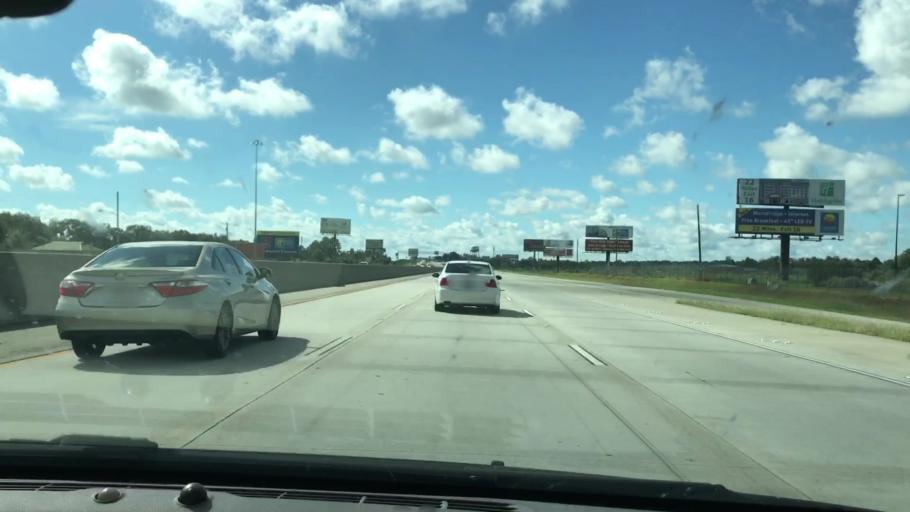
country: US
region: Georgia
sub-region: Cook County
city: Adel
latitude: 31.1336
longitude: -83.4384
